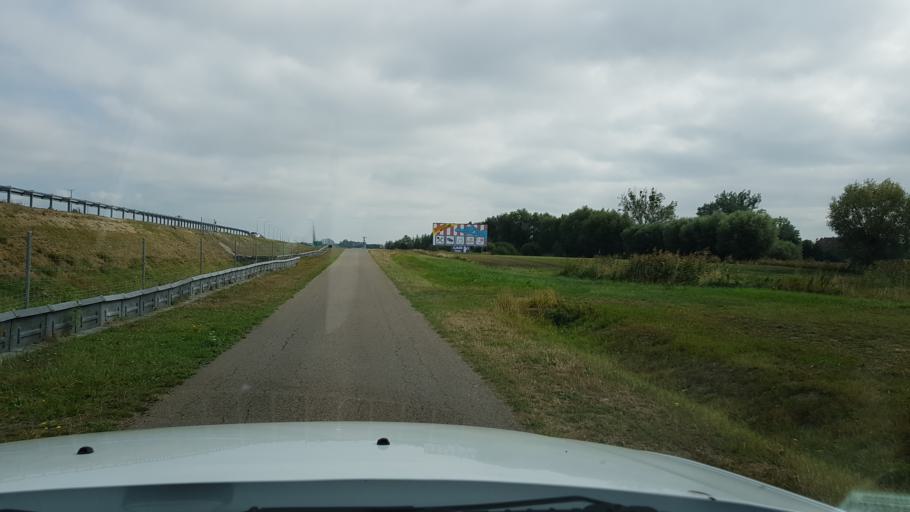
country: PL
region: West Pomeranian Voivodeship
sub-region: Powiat pyrzycki
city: Lipiany
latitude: 52.9576
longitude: 14.9324
